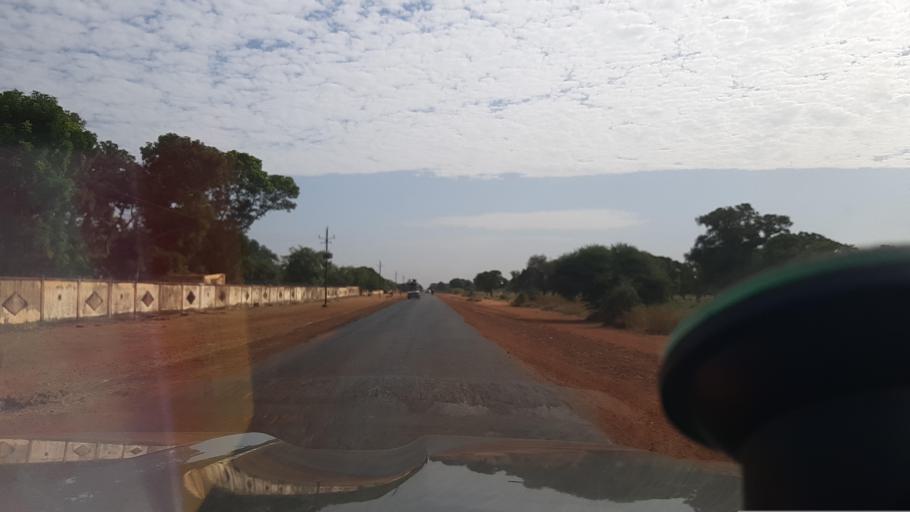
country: ML
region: Segou
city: Segou
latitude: 13.4976
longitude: -6.1613
